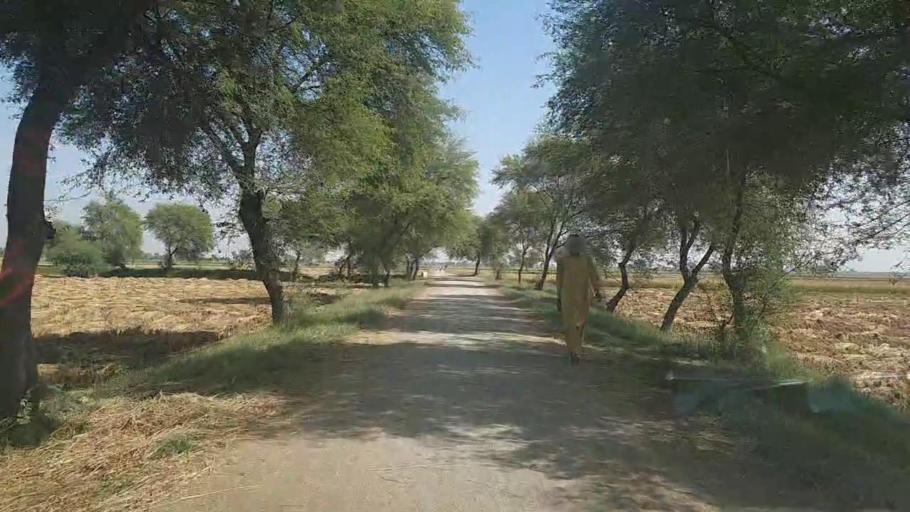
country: PK
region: Sindh
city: Thul
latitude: 28.2483
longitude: 68.8171
